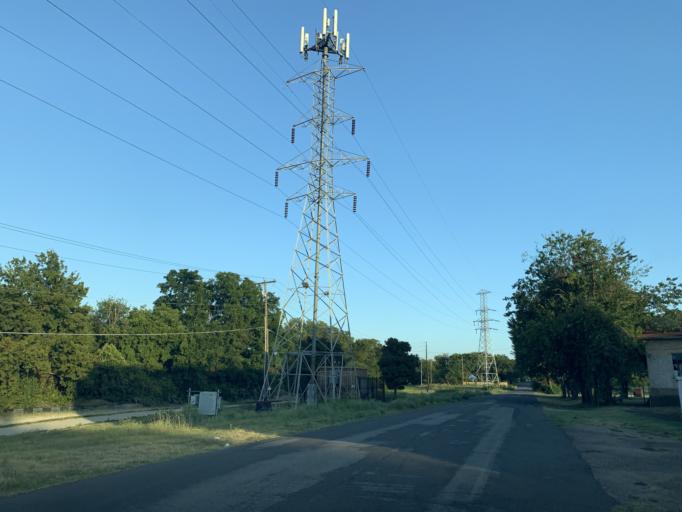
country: US
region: Texas
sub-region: Dallas County
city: Dallas
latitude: 32.7052
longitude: -96.8068
